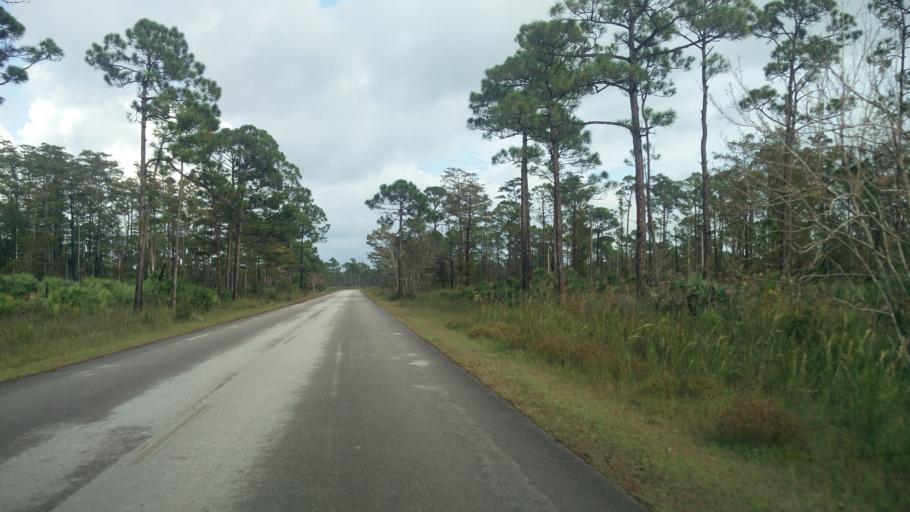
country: US
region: Florida
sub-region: Palm Beach County
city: Tequesta
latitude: 27.0069
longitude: -80.1368
